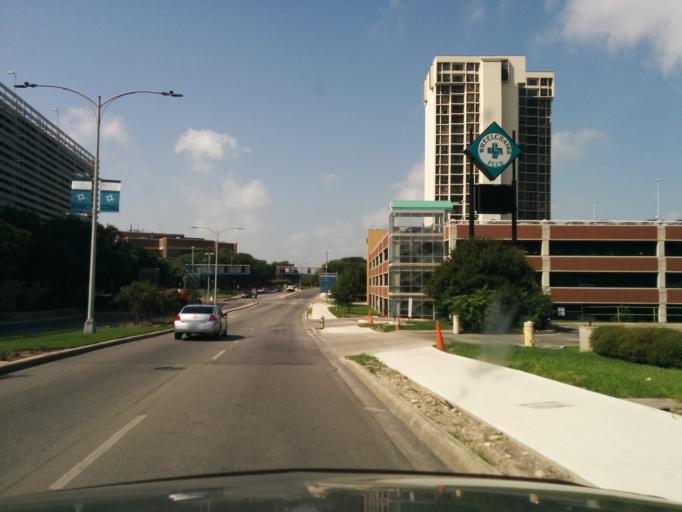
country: US
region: Texas
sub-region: Bexar County
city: Balcones Heights
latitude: 29.5096
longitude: -98.5806
